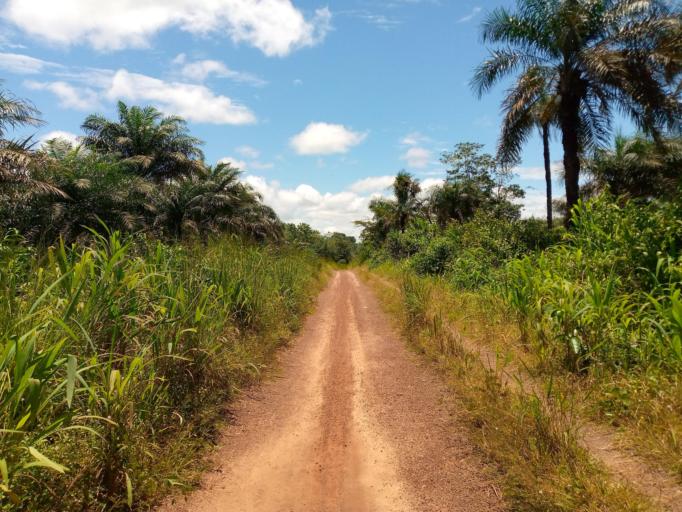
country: SL
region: Northern Province
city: Makeni
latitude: 9.0414
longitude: -12.1583
